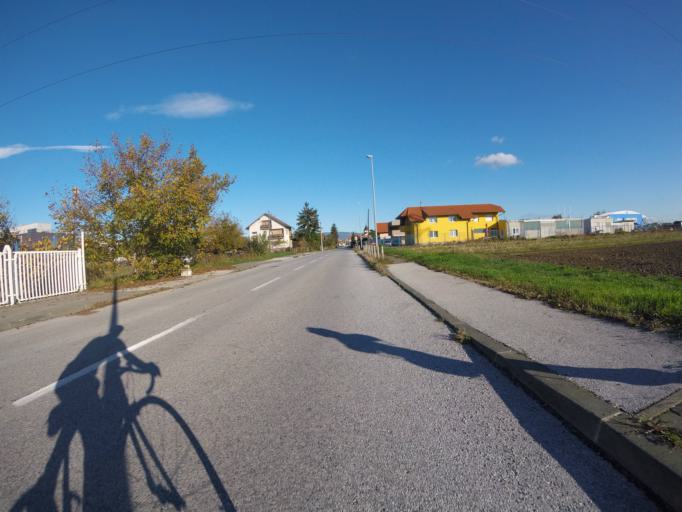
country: HR
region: Grad Zagreb
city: Odra
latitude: 45.7471
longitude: 15.9992
